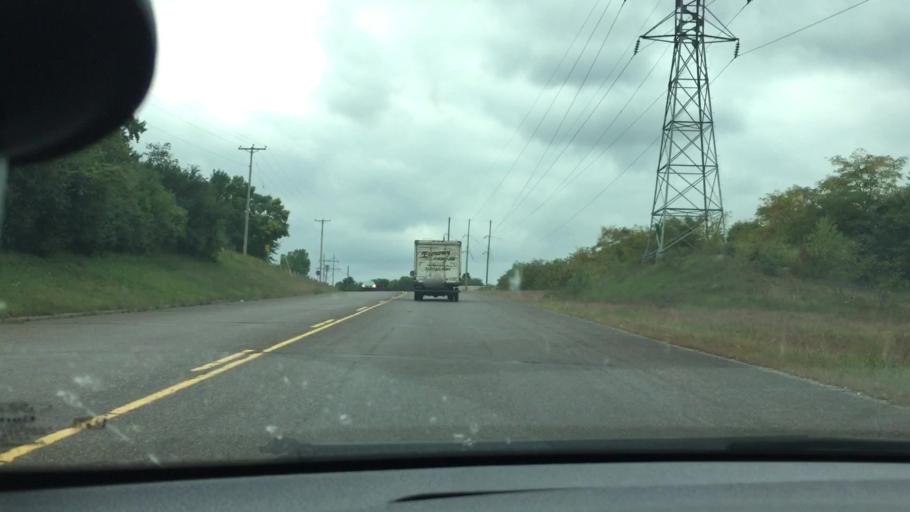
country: US
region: Wisconsin
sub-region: Chippewa County
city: Chippewa Falls
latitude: 44.9211
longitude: -91.3949
